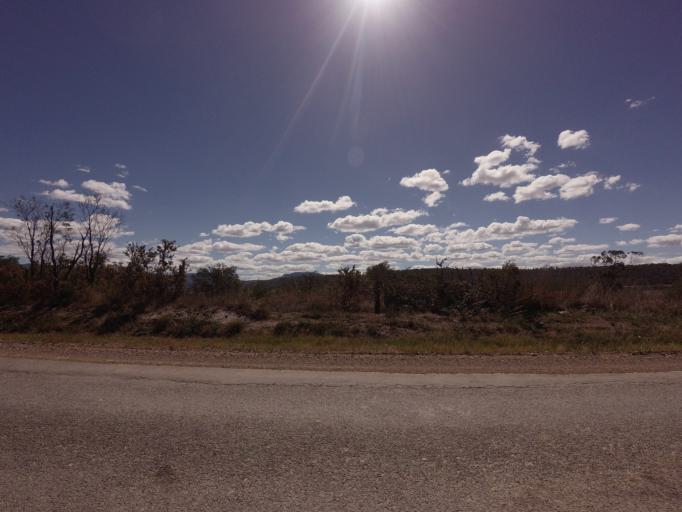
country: AU
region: Tasmania
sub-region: Break O'Day
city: St Helens
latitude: -41.6475
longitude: 147.9363
